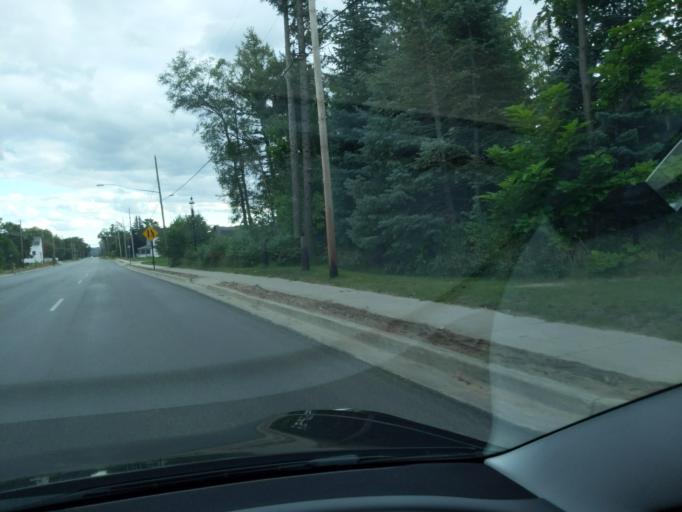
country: US
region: Michigan
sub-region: Kalkaska County
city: Rapid City
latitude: 44.8323
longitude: -85.2828
